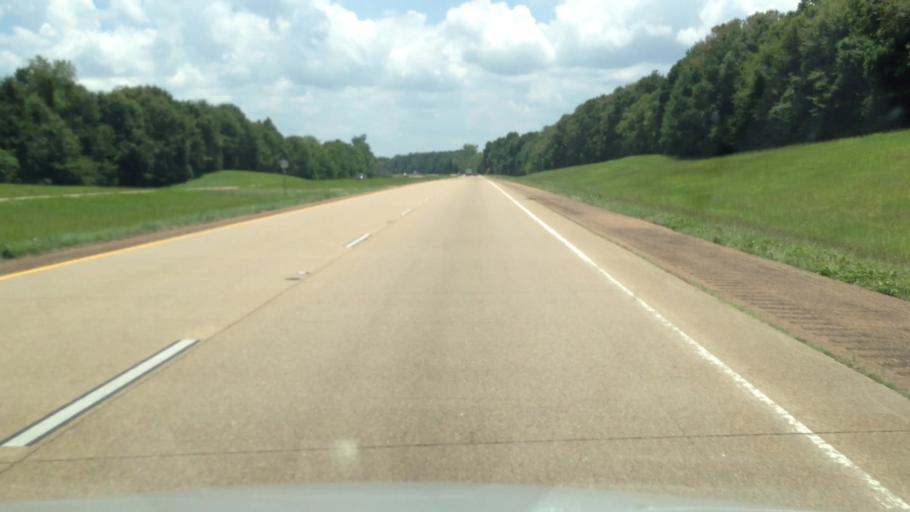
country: US
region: Louisiana
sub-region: Rapides Parish
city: Woodworth
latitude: 31.1494
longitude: -92.4534
